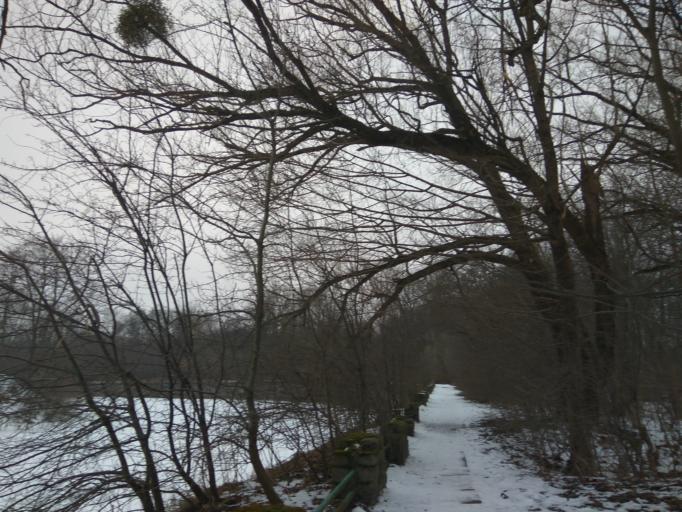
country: RU
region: Kaliningrad
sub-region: Gorod Kaliningrad
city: Kaliningrad
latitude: 54.7532
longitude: 20.4454
